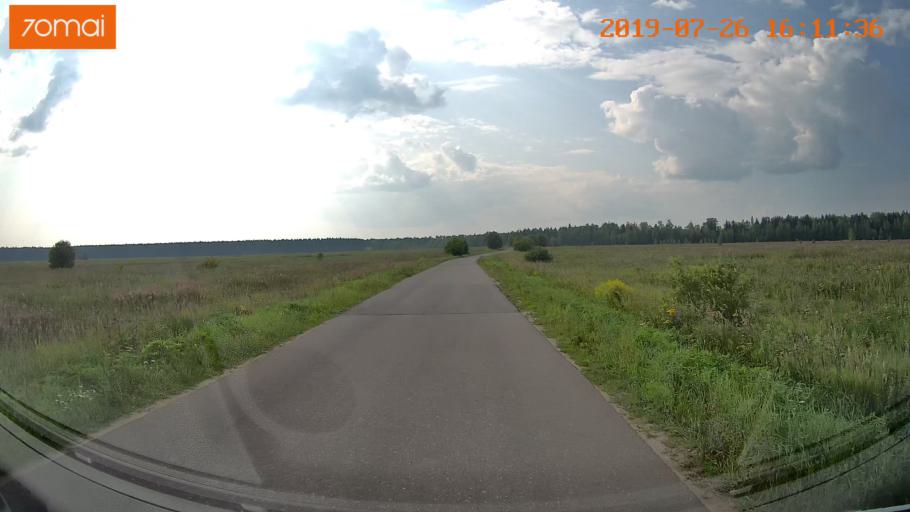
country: RU
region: Ivanovo
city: Bogorodskoye
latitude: 57.0659
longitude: 41.0597
